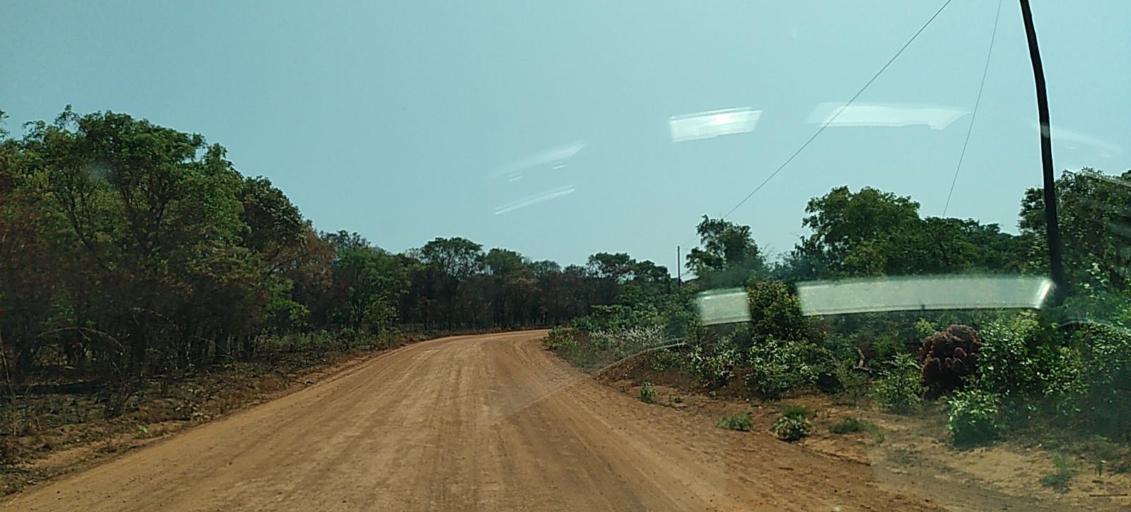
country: ZM
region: North-Western
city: Kansanshi
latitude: -11.9932
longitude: 26.6173
